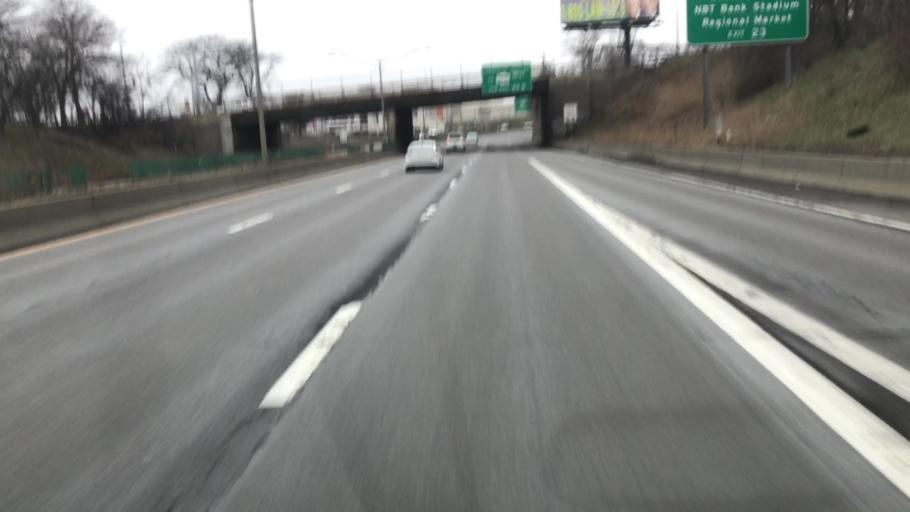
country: US
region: New York
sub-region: Onondaga County
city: Syracuse
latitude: 43.0660
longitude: -76.1627
